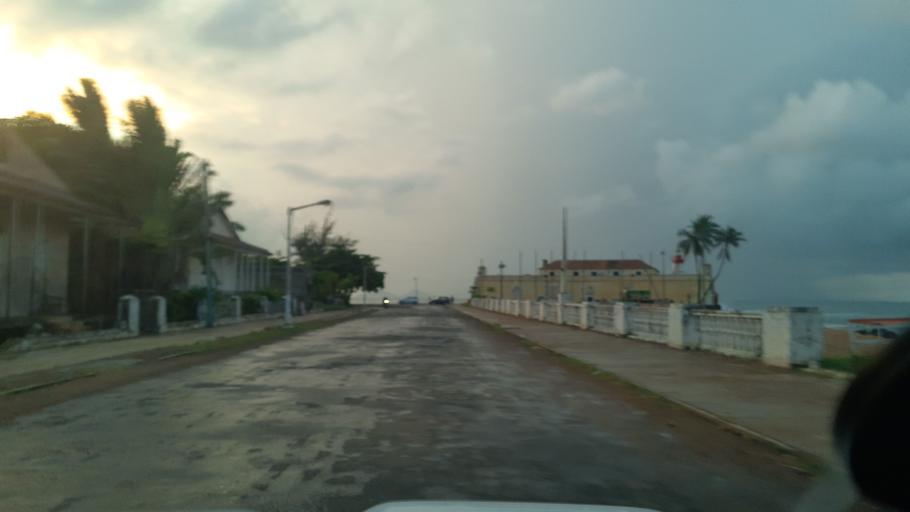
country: ST
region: Sao Tome Island
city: Sao Tome
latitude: 0.3444
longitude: 6.7395
